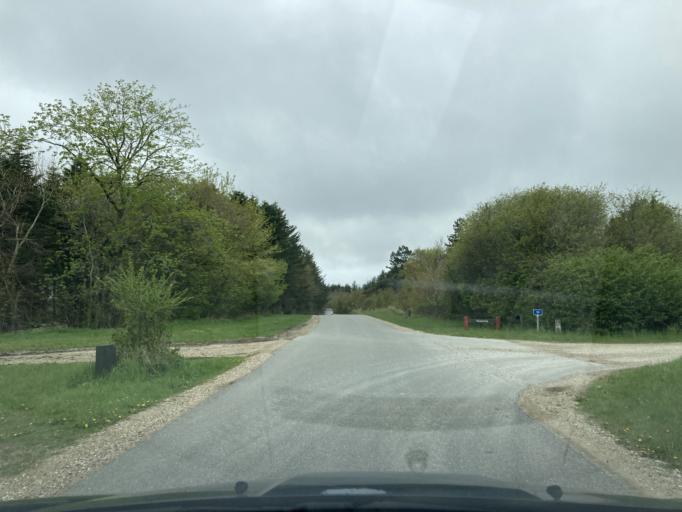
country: DK
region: North Denmark
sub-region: Thisted Kommune
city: Hurup
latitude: 56.8160
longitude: 8.3025
